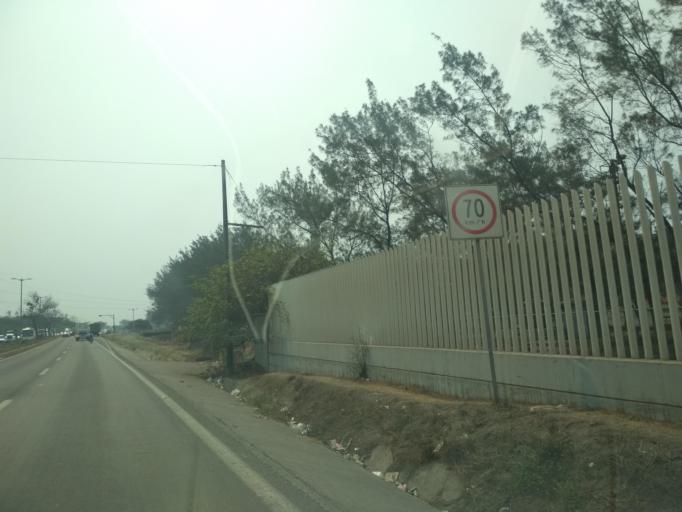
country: MX
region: Veracruz
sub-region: Veracruz
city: Oasis
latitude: 19.1753
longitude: -96.2386
